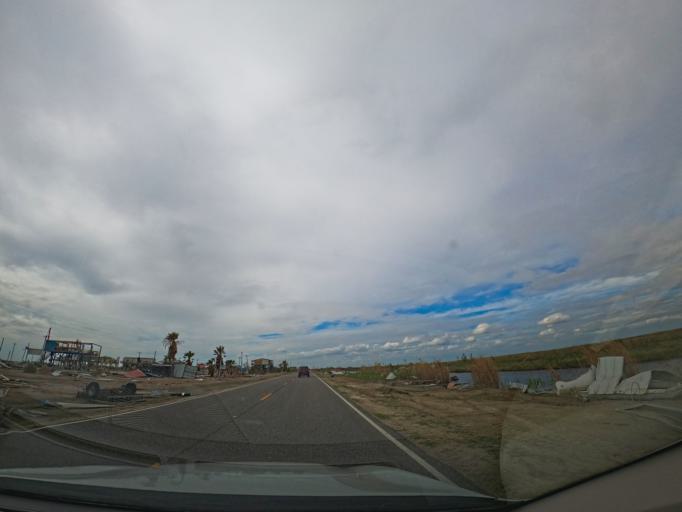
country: US
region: Louisiana
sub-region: Cameron Parish
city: Cameron
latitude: 29.7719
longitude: -93.4478
